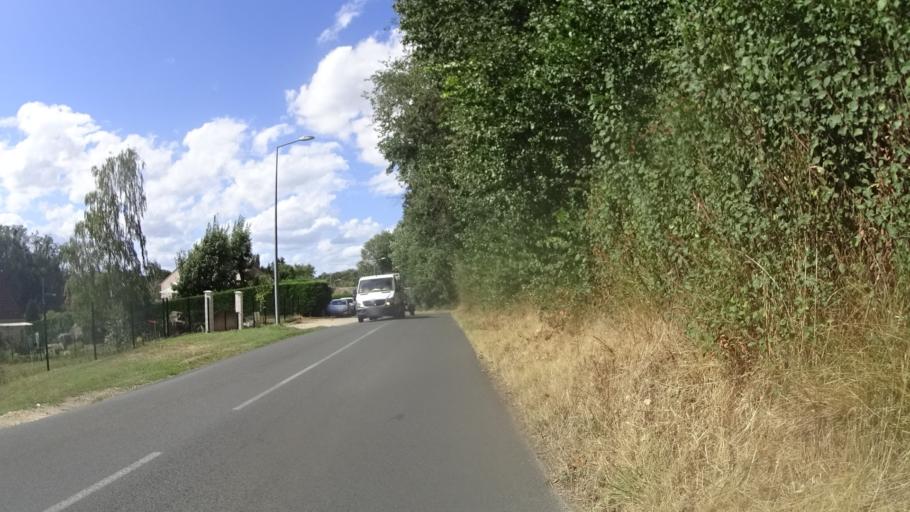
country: FR
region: Ile-de-France
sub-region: Departement de l'Essonne
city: Boutigny-sur-Essonne
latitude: 48.4513
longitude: 2.3659
